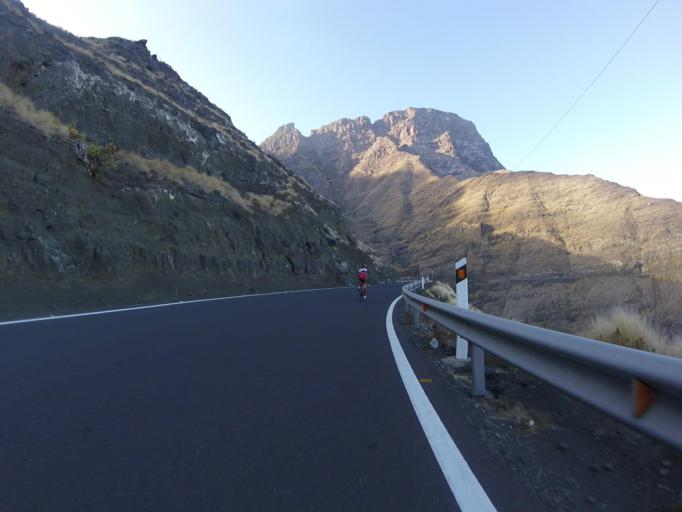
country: ES
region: Canary Islands
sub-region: Provincia de Las Palmas
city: Agaete
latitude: 28.0740
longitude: -15.7103
